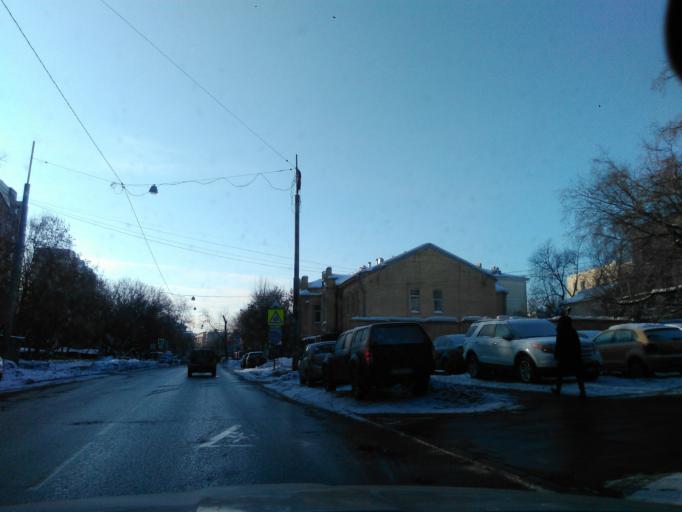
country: RU
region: Moscow
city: Mar'ina Roshcha
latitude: 55.7990
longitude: 37.5821
